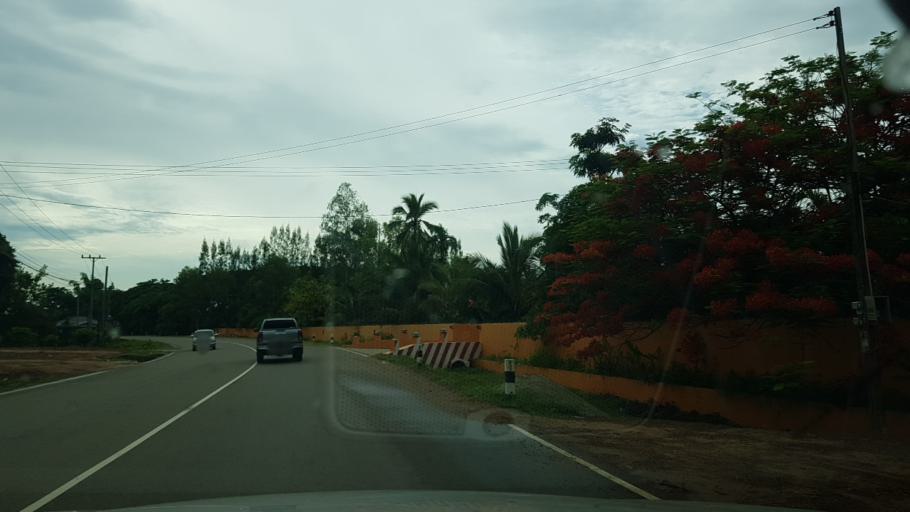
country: TH
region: Nong Khai
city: Si Chiang Mai
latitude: 17.9745
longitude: 102.4865
